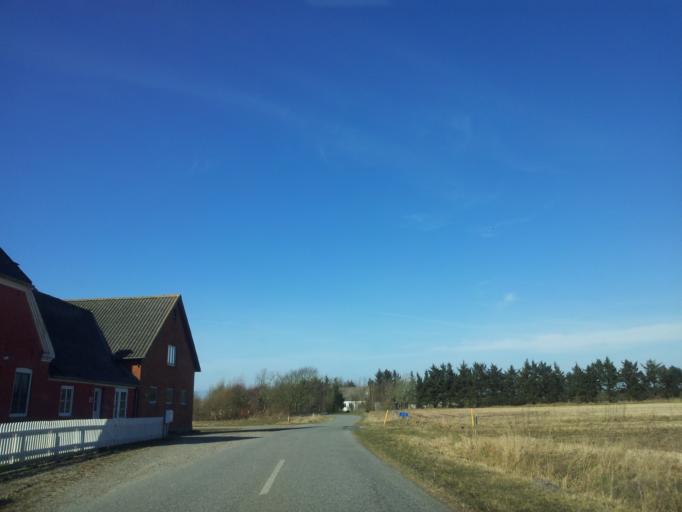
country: DK
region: South Denmark
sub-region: Tonder Kommune
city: Sherrebek
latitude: 55.1793
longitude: 8.7184
